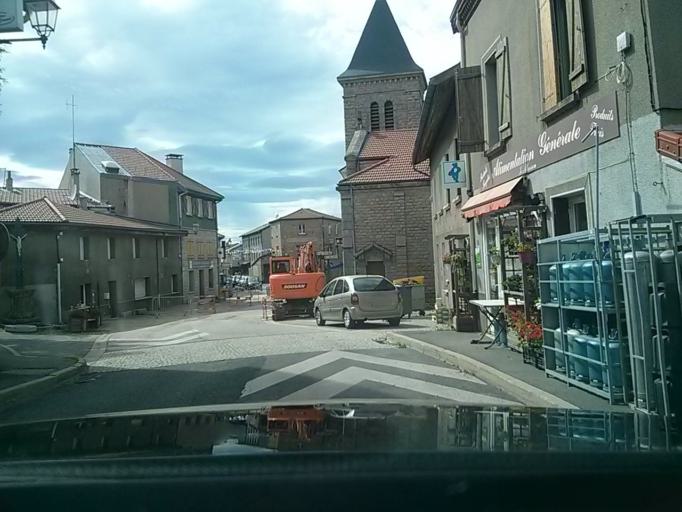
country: FR
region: Rhone-Alpes
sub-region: Departement de la Loire
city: Bourg-Argental
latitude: 45.3682
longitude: 4.5172
